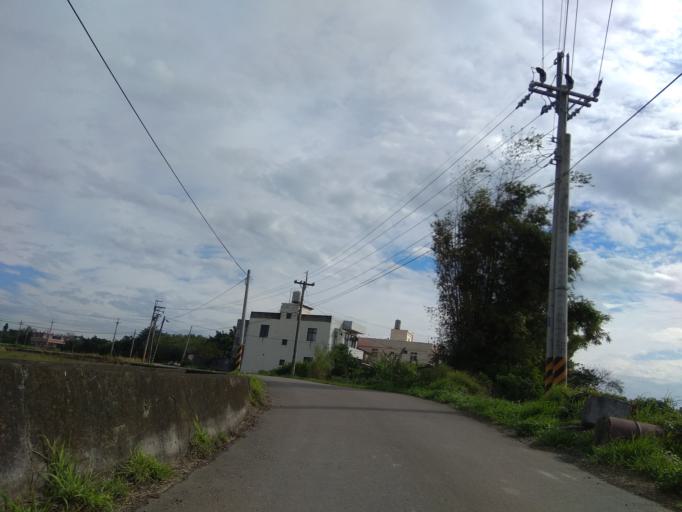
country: TW
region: Taiwan
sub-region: Hsinchu
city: Zhubei
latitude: 24.9480
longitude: 121.1074
